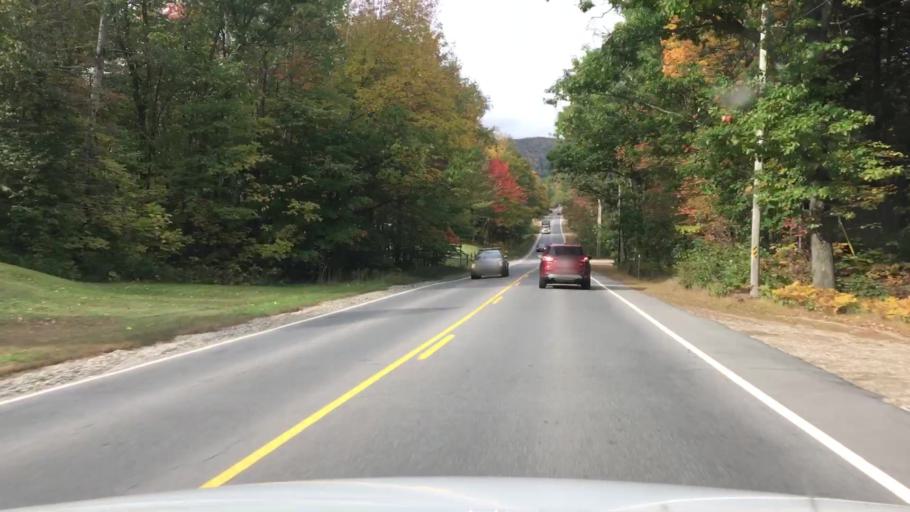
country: US
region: New Hampshire
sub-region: Coos County
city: Gorham
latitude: 44.3861
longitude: -71.1466
